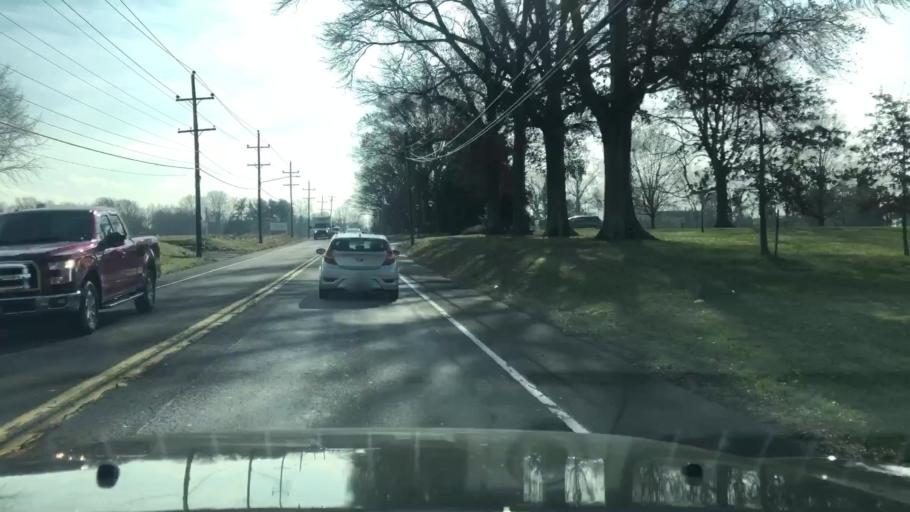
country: US
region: Pennsylvania
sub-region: Bucks County
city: Newtown
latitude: 40.2121
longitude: -74.9307
